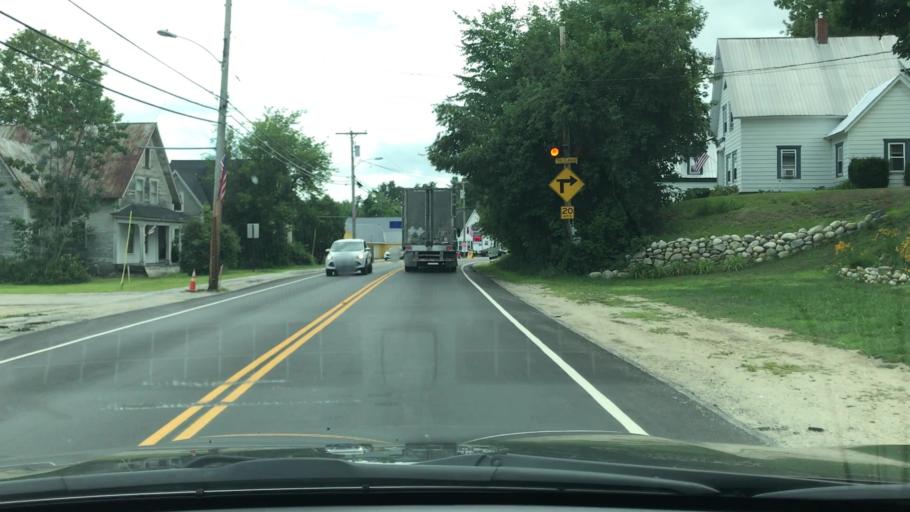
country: US
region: Maine
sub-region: Oxford County
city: West Paris
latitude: 44.3797
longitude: -70.6441
